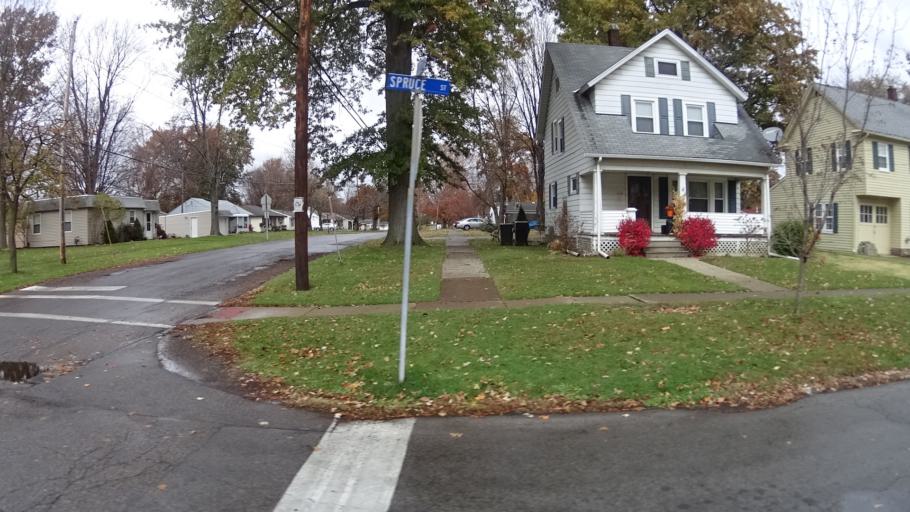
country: US
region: Ohio
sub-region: Lorain County
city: Elyria
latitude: 41.3796
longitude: -82.1316
